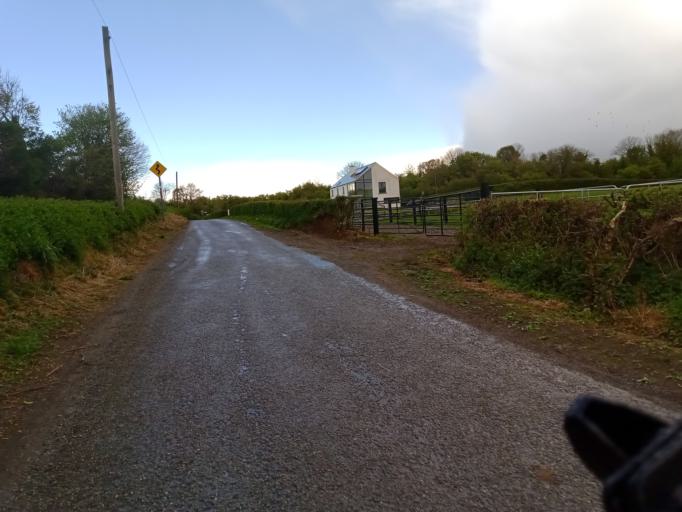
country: IE
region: Leinster
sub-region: Kilkenny
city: Kilkenny
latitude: 52.6930
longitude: -7.2710
